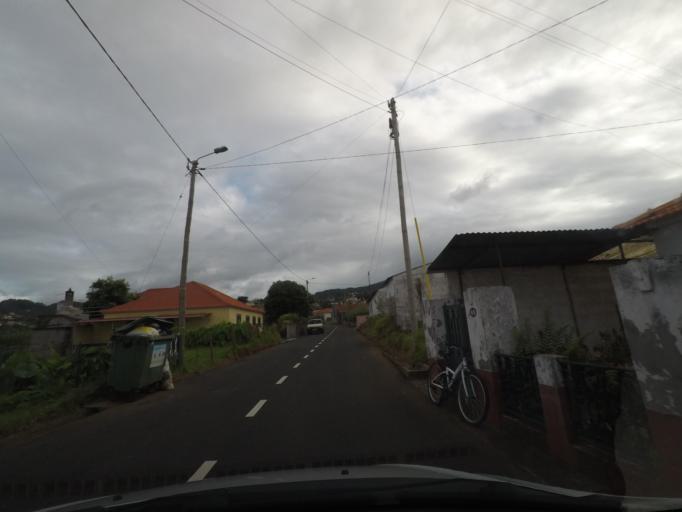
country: PT
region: Madeira
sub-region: Santana
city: Santana
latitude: 32.8105
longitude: -16.8765
